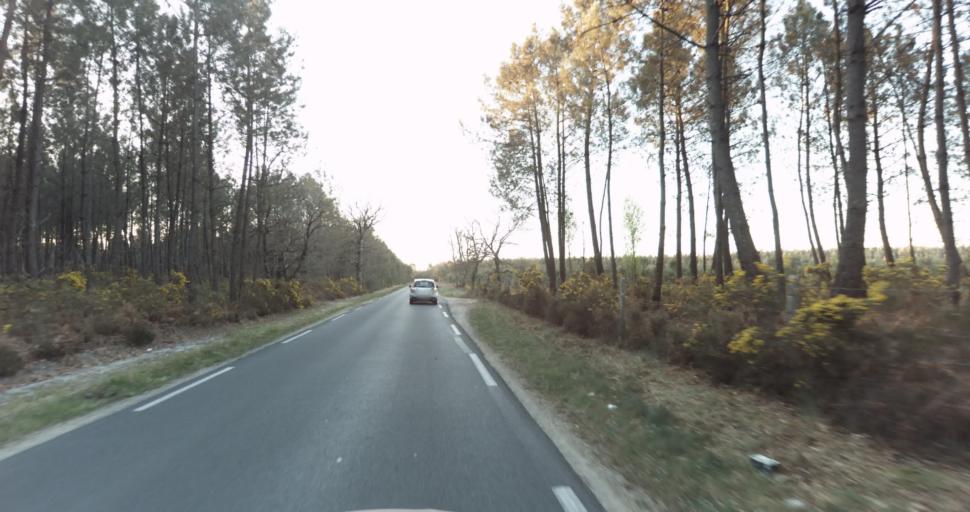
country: FR
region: Aquitaine
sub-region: Departement de la Gironde
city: Martignas-sur-Jalle
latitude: 44.8294
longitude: -0.7653
